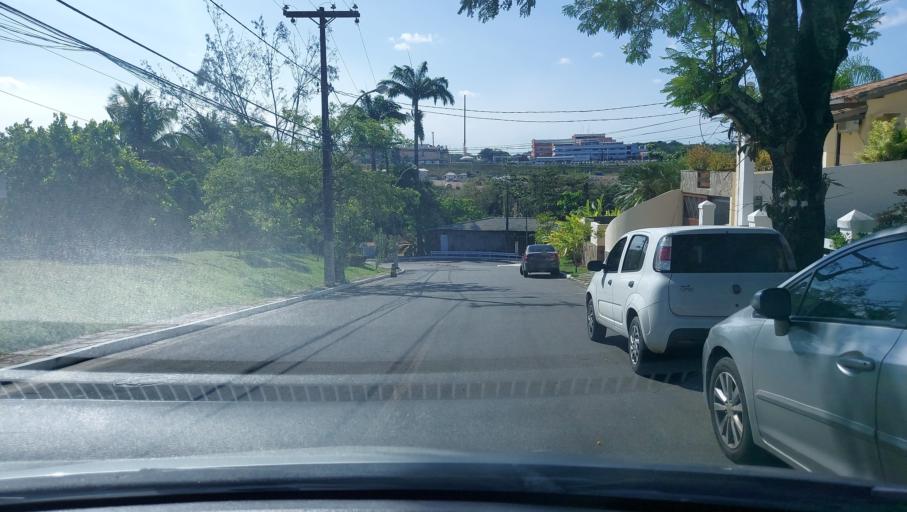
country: BR
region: Bahia
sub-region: Lauro De Freitas
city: Lauro de Freitas
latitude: -12.9409
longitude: -38.3821
